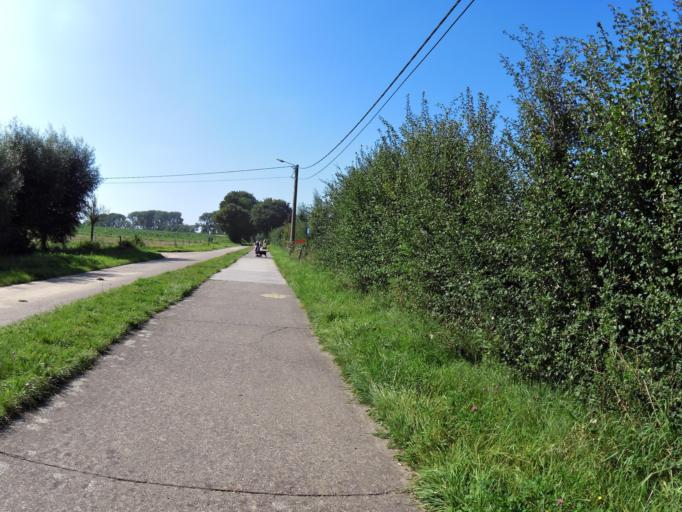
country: BE
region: Flanders
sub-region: Provincie Limburg
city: Tongeren
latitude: 50.7715
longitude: 5.5106
